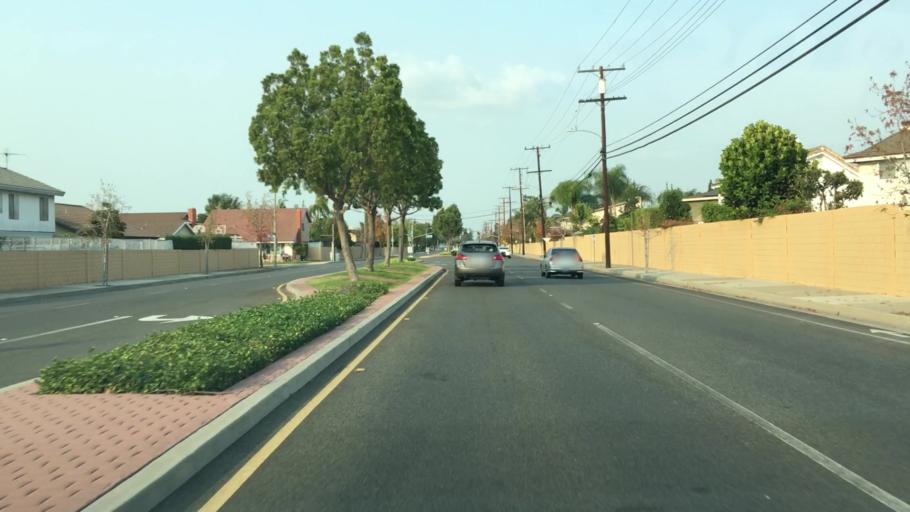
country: US
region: California
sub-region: Orange County
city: La Palma
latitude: 33.8509
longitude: -118.0460
